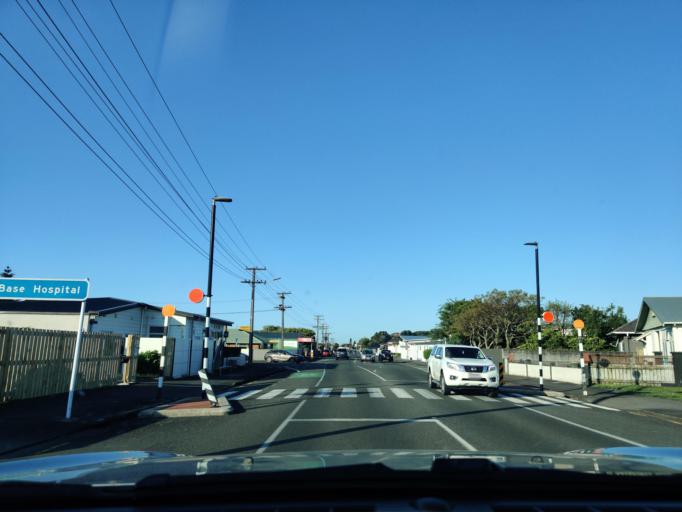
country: NZ
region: Taranaki
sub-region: New Plymouth District
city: New Plymouth
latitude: -39.0743
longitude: 174.0583
